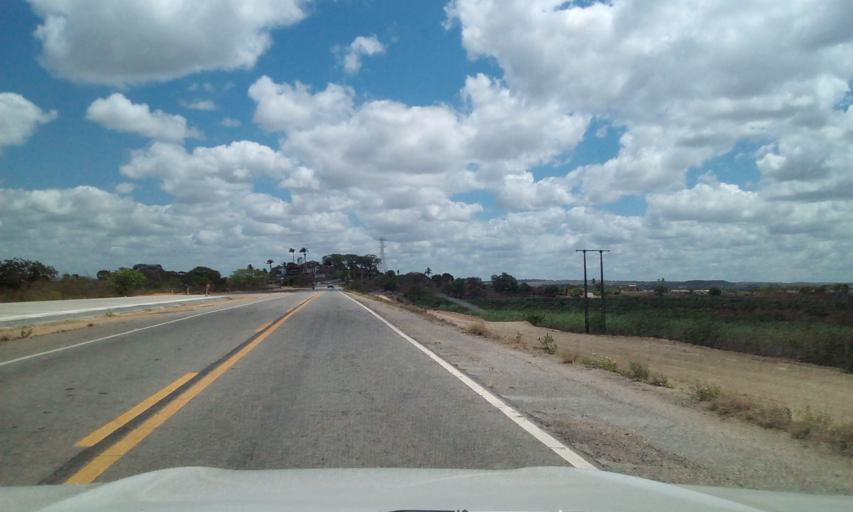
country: BR
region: Sergipe
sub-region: Propria
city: Propria
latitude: -10.2193
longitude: -36.8268
